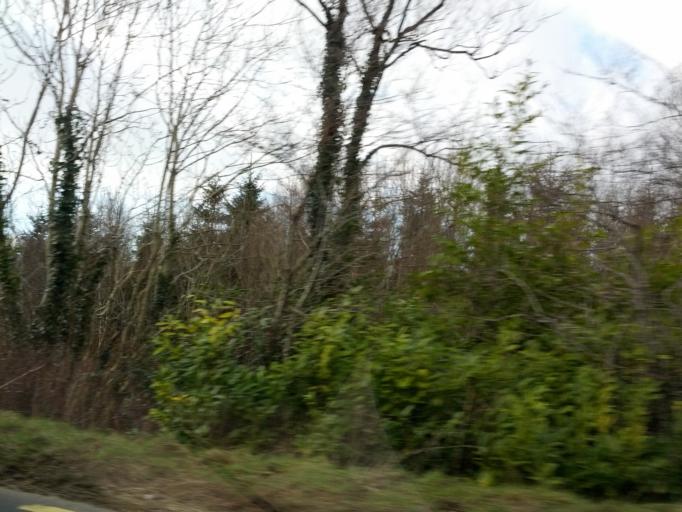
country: IE
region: Connaught
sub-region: County Galway
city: Athenry
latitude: 53.4540
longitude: -8.6927
